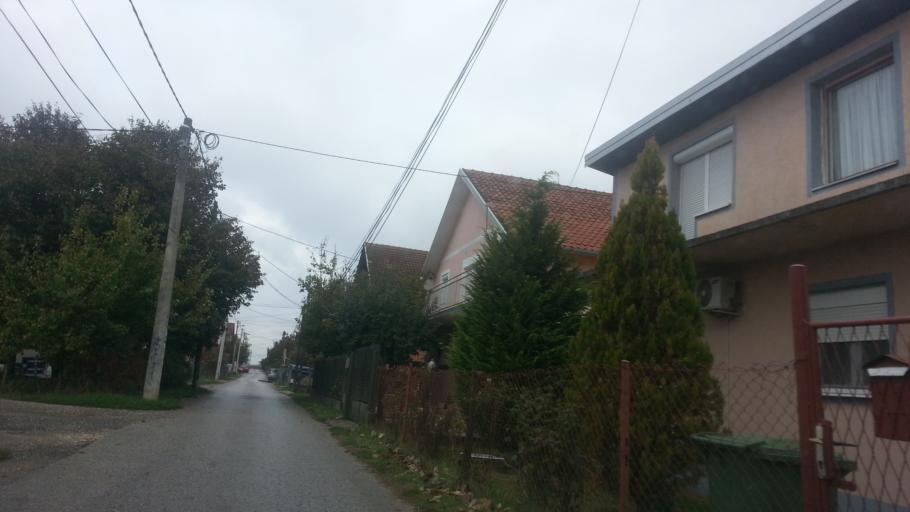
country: RS
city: Novi Banovci
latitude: 44.9121
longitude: 20.2893
